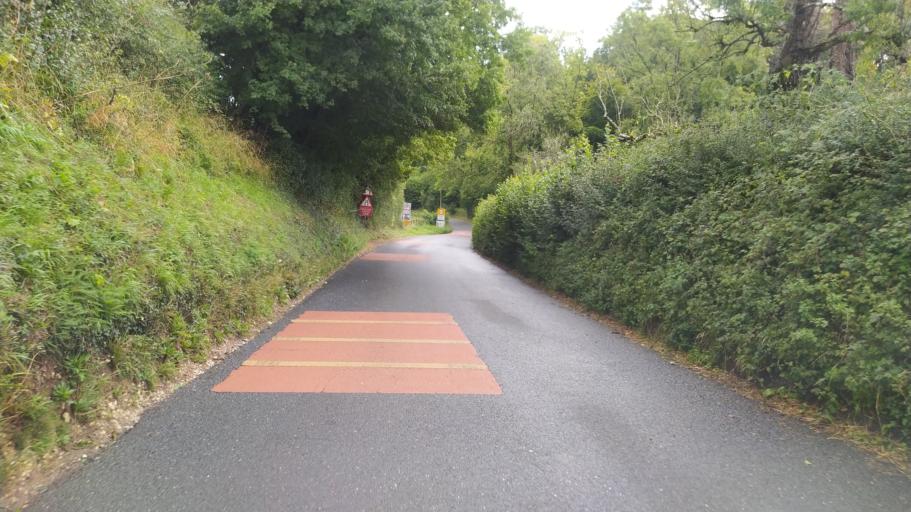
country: GB
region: England
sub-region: Wiltshire
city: Ansty
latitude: 50.9597
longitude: -2.0861
